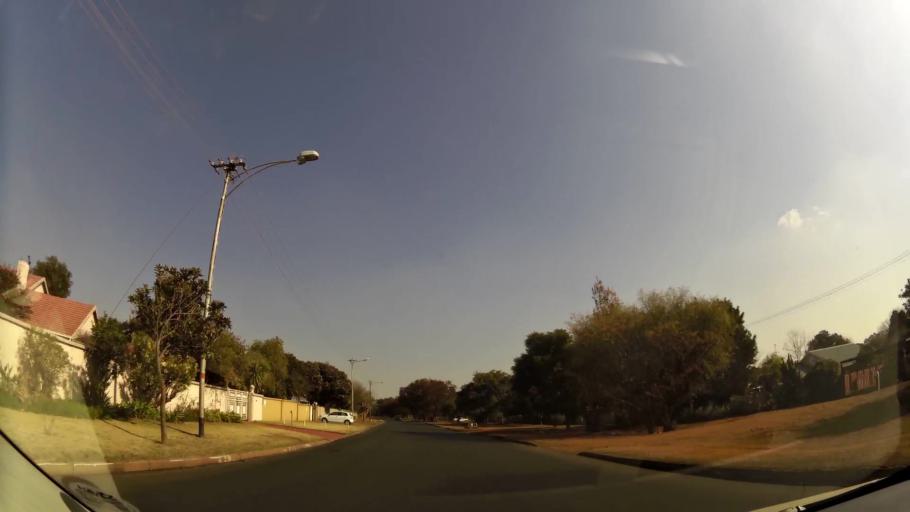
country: ZA
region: Gauteng
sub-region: West Rand District Municipality
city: Randfontein
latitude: -26.1617
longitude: 27.6915
